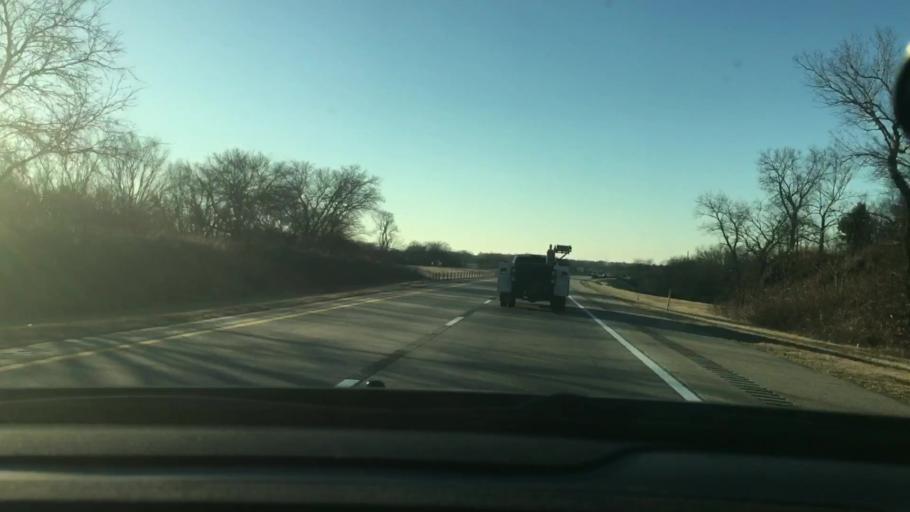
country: US
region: Oklahoma
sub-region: Murray County
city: Davis
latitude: 34.3507
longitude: -97.1484
